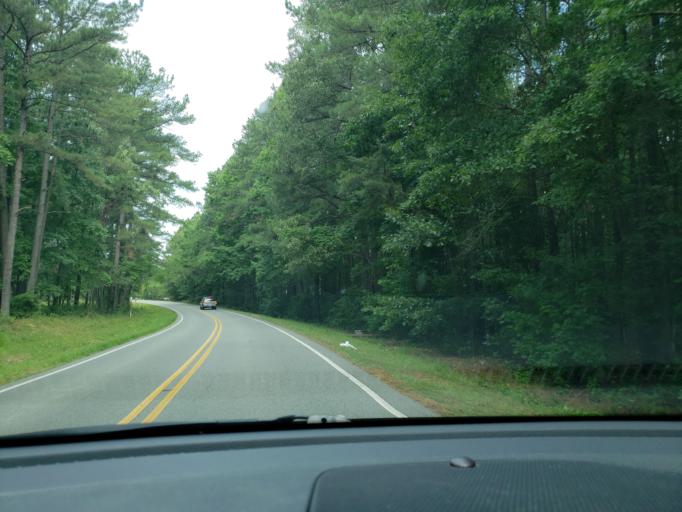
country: US
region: North Carolina
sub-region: Wake County
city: Green Level
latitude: 35.7950
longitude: -78.9753
